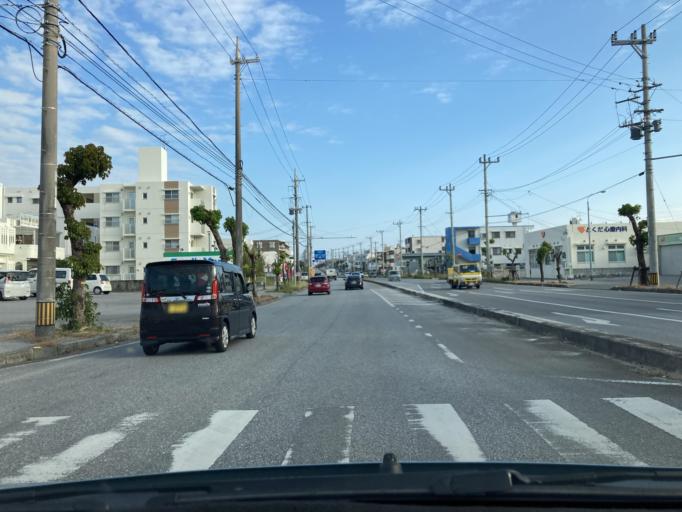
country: JP
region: Okinawa
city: Okinawa
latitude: 26.3503
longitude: 127.8302
